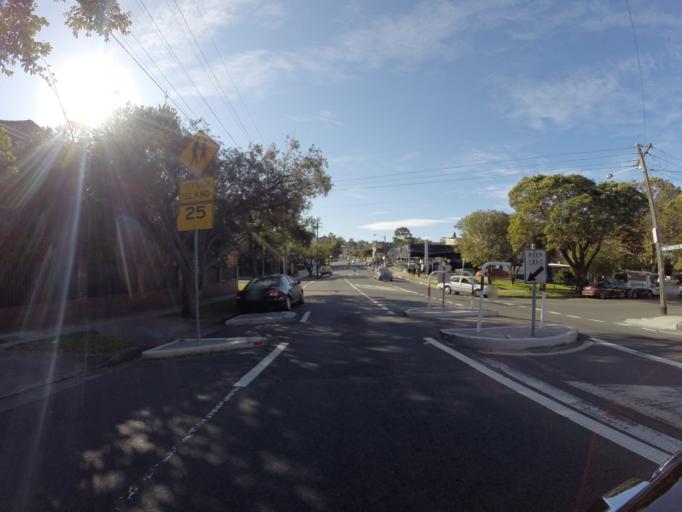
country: AU
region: New South Wales
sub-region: Randwick
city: Randwick
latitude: -33.9177
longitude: 151.2486
